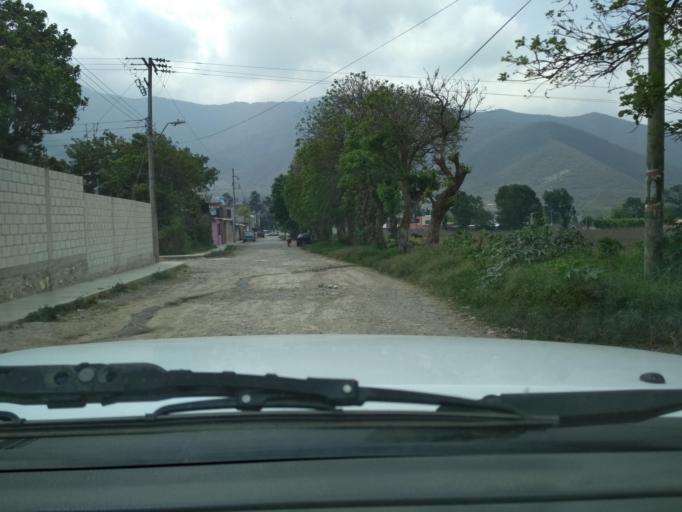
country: MX
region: Veracruz
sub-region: Acultzingo
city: Acatla
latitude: 18.7629
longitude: -97.2223
